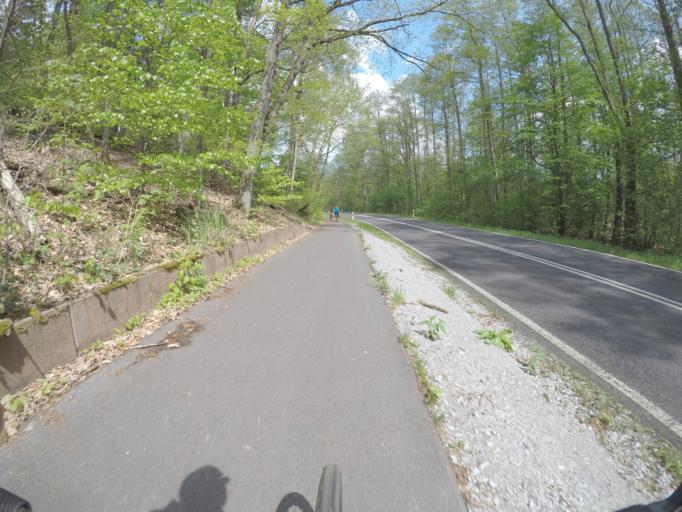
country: DE
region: Brandenburg
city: Joachimsthal
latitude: 52.9245
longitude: 13.7040
